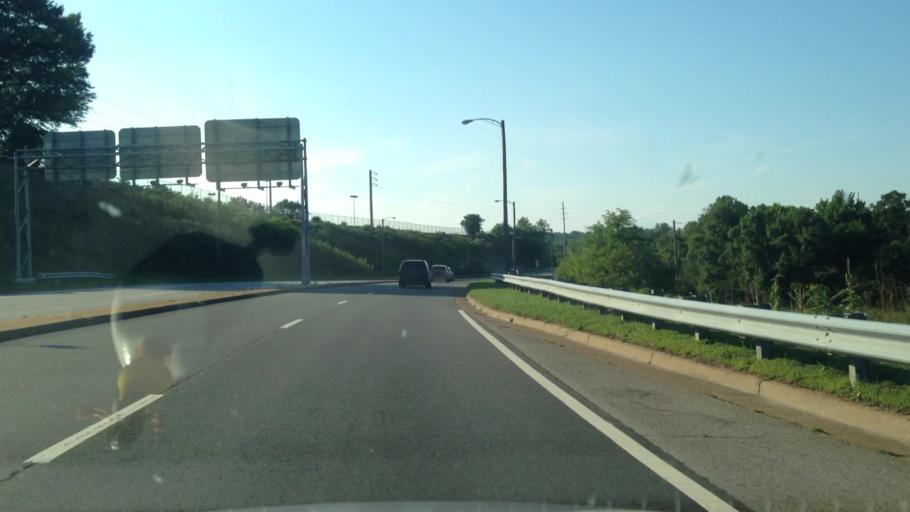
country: US
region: Virginia
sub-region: City of Danville
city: Danville
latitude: 36.5928
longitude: -79.4174
